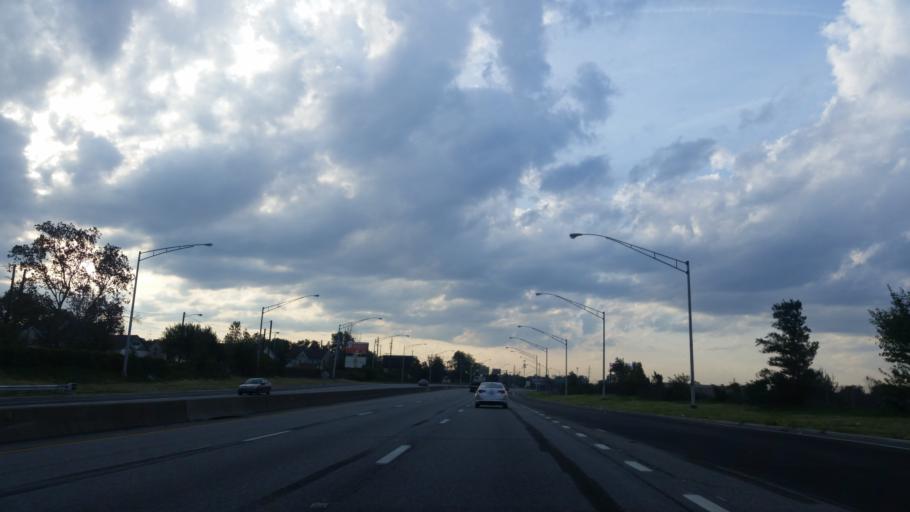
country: US
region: Ohio
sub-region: Cuyahoga County
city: Newburgh Heights
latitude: 41.4684
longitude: -81.6593
